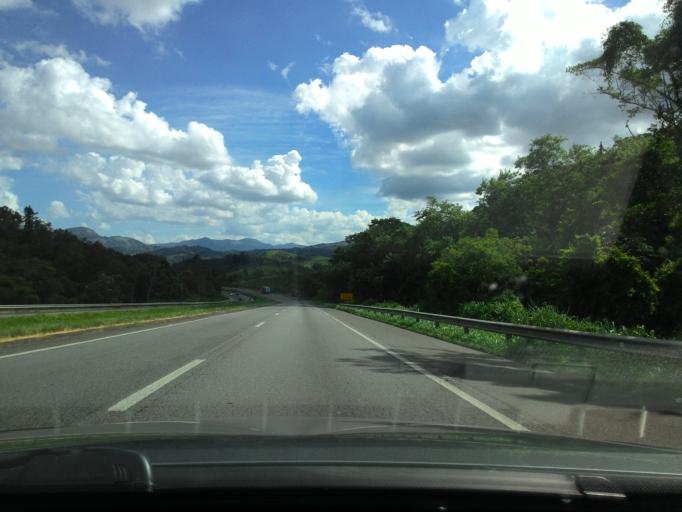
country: BR
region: Sao Paulo
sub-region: Cajati
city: Cajati
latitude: -24.7659
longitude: -48.1675
